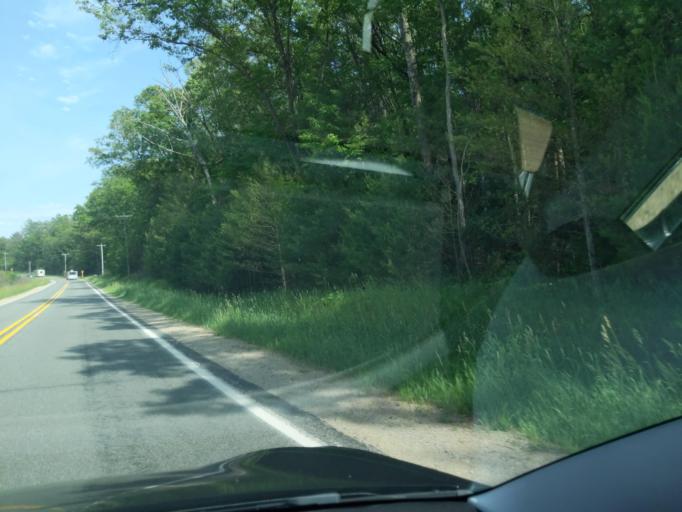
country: US
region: Michigan
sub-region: Muskegon County
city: Lakewood Club
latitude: 43.4093
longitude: -86.2890
